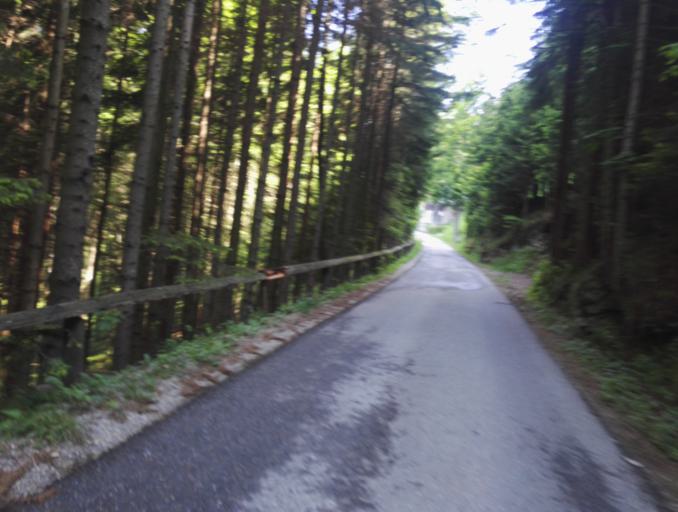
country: AT
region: Styria
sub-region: Politischer Bezirk Graz-Umgebung
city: Semriach
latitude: 47.1897
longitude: 15.4278
